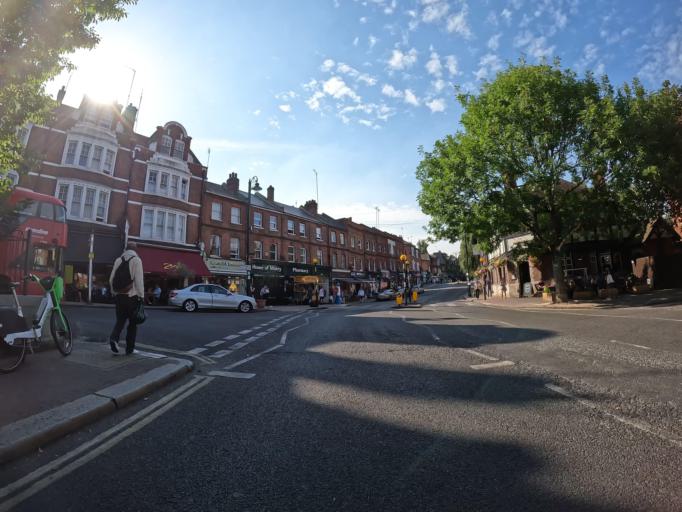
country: GB
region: England
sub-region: Greater London
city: Hendon
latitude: 51.6153
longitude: -0.2170
